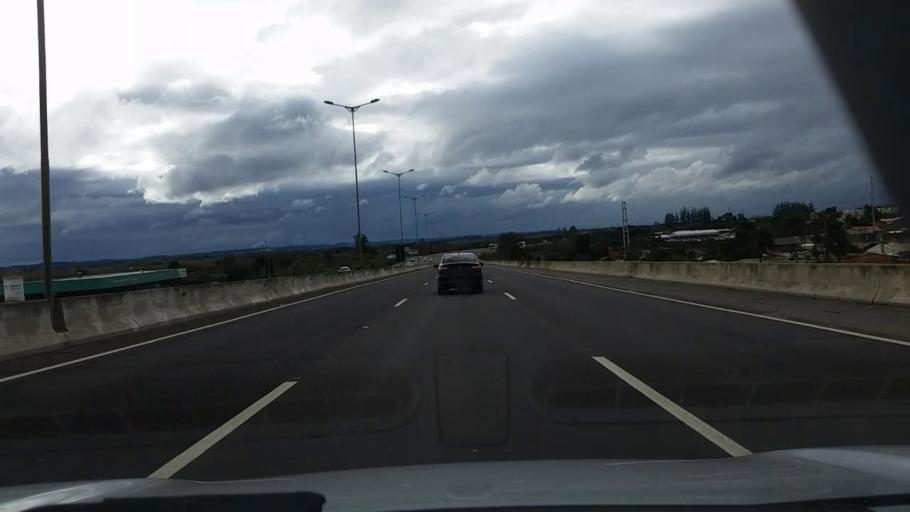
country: BR
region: Rio Grande do Sul
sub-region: Canoas
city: Canoas
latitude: -29.9675
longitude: -51.2014
